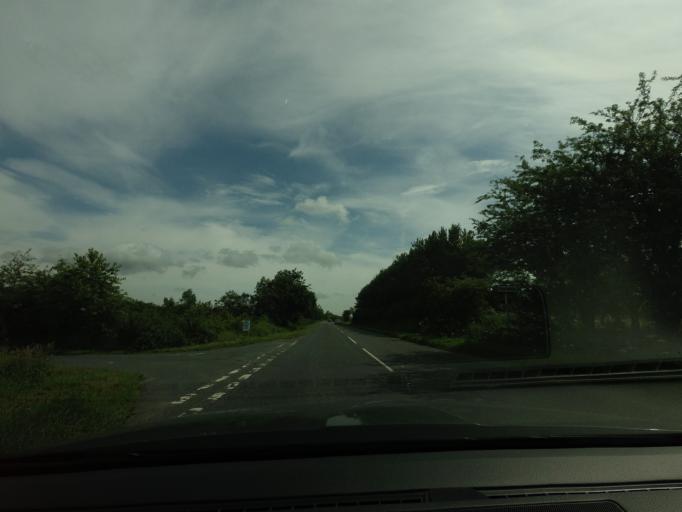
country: GB
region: Scotland
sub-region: Aberdeenshire
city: Mintlaw
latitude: 57.5249
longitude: -1.9834
